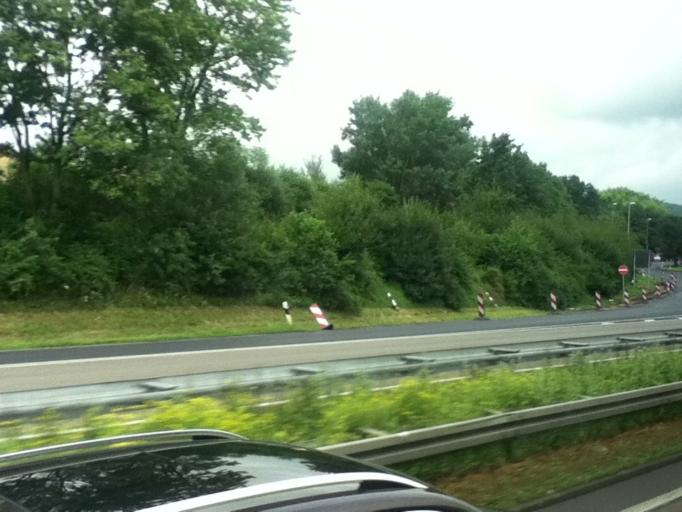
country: DE
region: Hesse
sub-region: Regierungsbezirk Kassel
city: Ottrau
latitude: 50.7584
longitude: 9.3554
